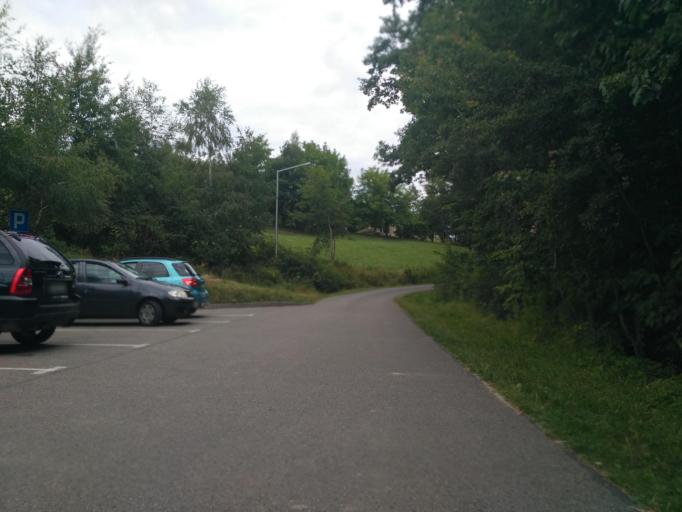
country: PL
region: Subcarpathian Voivodeship
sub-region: Powiat rzeszowski
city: Straszydle
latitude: 49.8925
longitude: 21.9417
